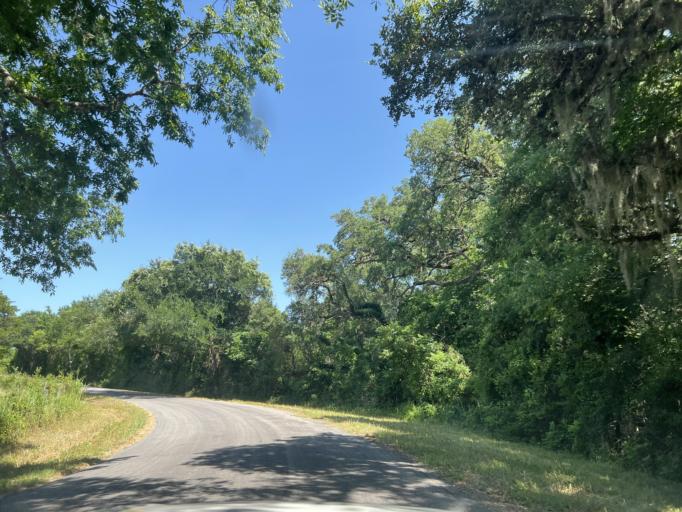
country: US
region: Texas
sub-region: Washington County
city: Brenham
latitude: 30.1710
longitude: -96.5065
